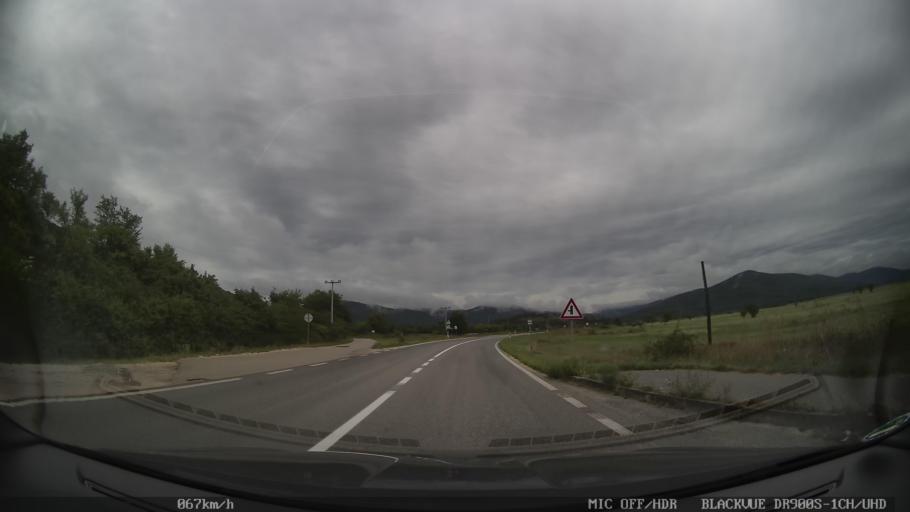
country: HR
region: Licko-Senjska
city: Otocac
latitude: 44.8612
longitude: 15.3057
